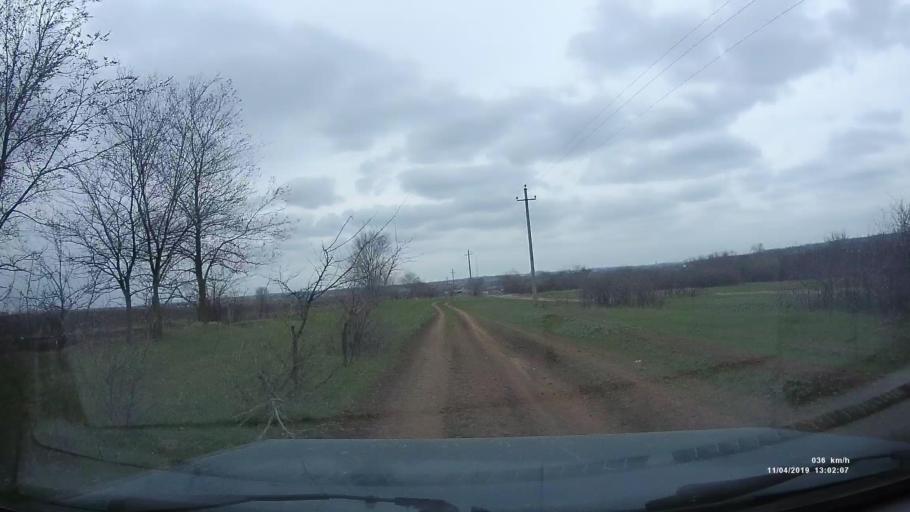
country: RU
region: Rostov
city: Staraya Stanitsa
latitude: 48.2876
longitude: 40.3610
